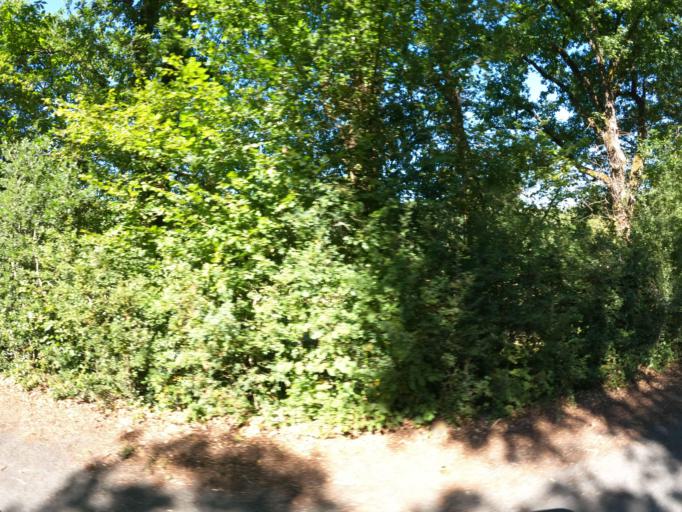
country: FR
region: Pays de la Loire
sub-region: Departement de la Vendee
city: Saint-Aubin-des-Ormeaux
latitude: 47.0031
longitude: -1.0175
